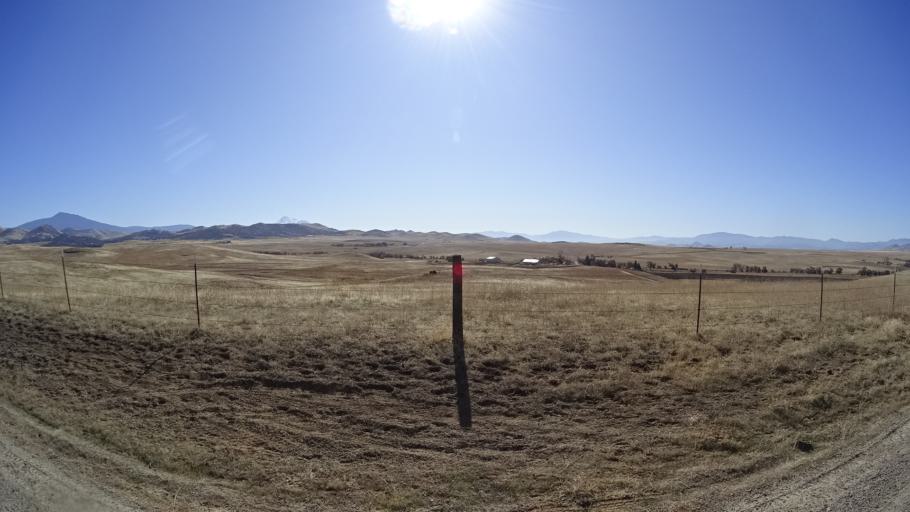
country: US
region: California
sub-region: Siskiyou County
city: Montague
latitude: 41.8299
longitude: -122.4181
